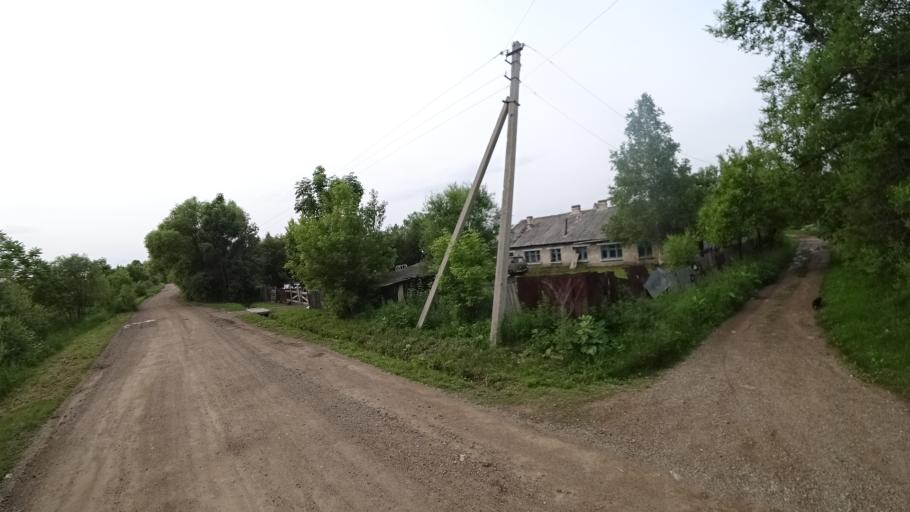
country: RU
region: Primorskiy
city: Novosysoyevka
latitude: 44.2430
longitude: 133.3624
